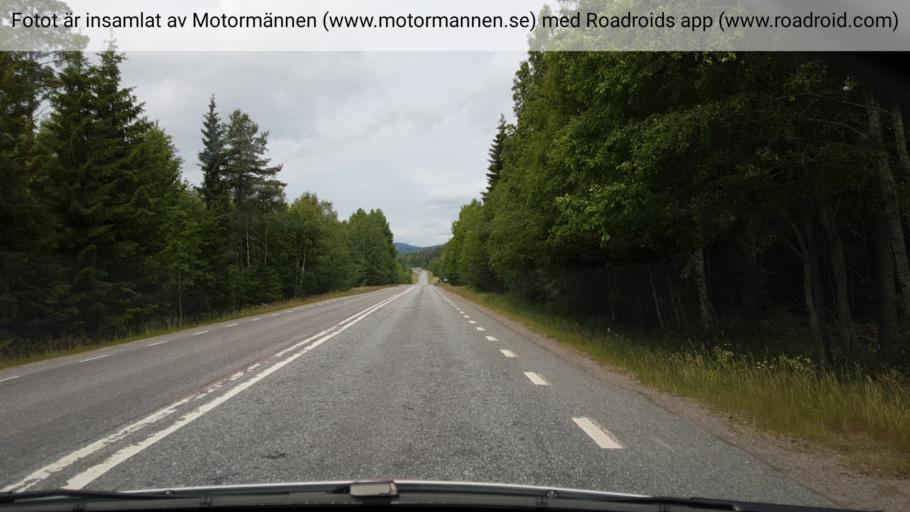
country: SE
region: Vaesternorrland
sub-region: Solleftea Kommun
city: Solleftea
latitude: 63.3149
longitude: 17.1945
